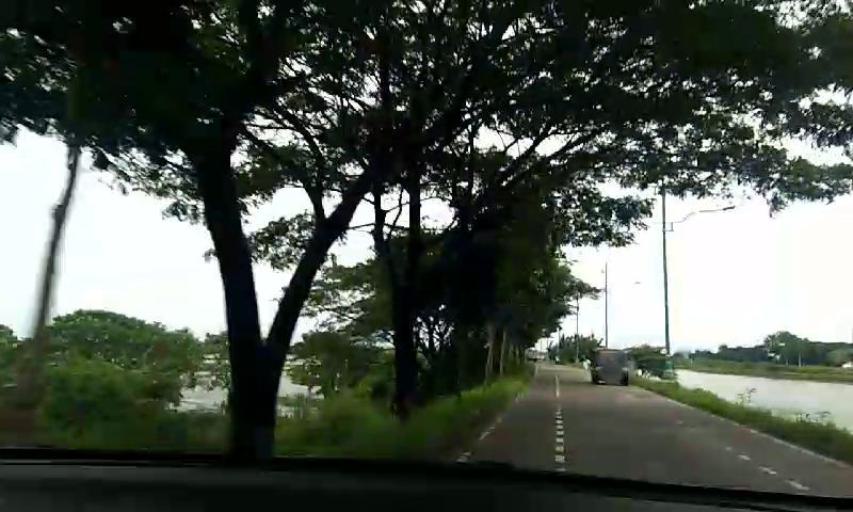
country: ID
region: West Java
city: Bekasi
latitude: -6.1272
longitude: 106.9692
